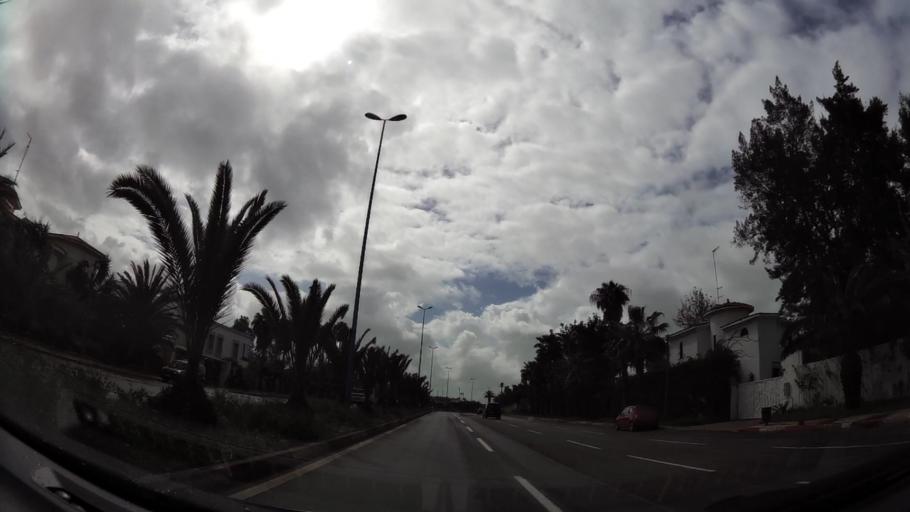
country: MA
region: Grand Casablanca
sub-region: Casablanca
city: Casablanca
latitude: 33.5305
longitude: -7.6253
